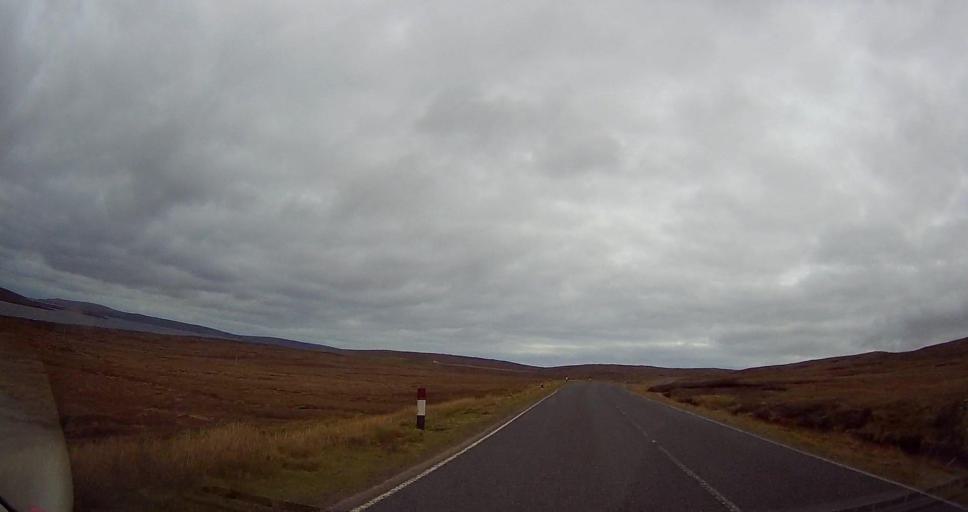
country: GB
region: Scotland
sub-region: Shetland Islands
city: Shetland
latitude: 60.6423
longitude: -1.0708
